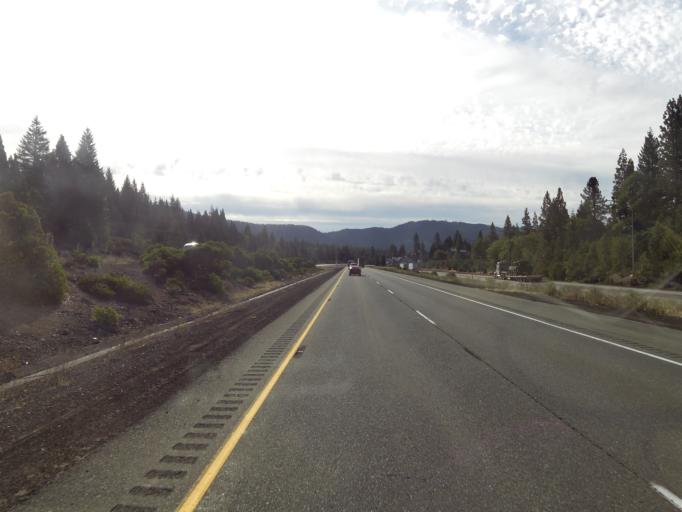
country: US
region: California
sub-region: Siskiyou County
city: Mount Shasta
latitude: 41.2738
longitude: -122.2841
